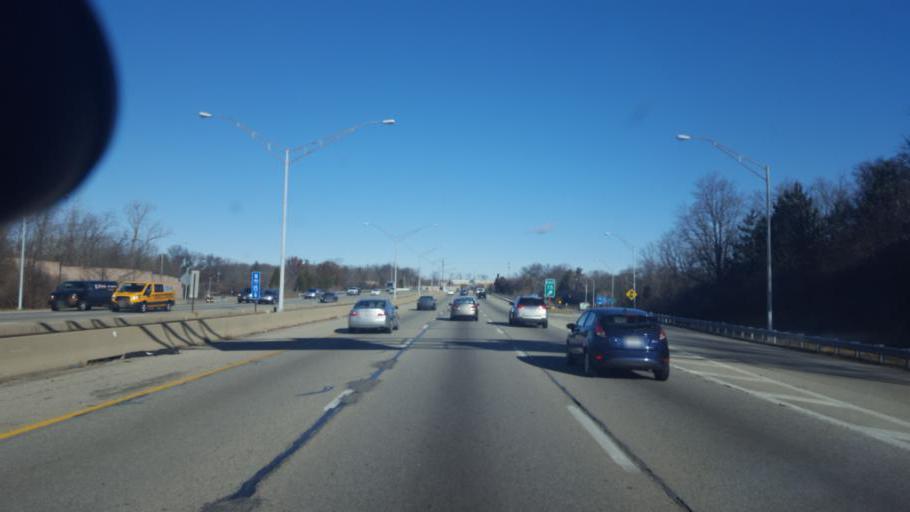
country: US
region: Ohio
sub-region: Hamilton County
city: Blue Ash
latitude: 39.2465
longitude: -84.3657
